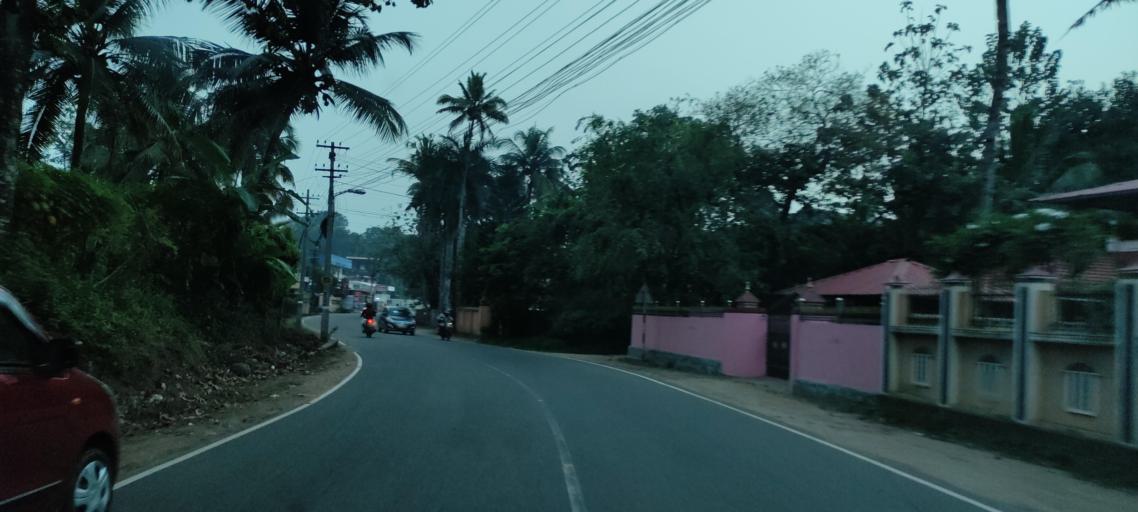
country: IN
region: Kerala
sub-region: Pattanamtitta
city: Adur
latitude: 9.1611
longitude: 76.7436
